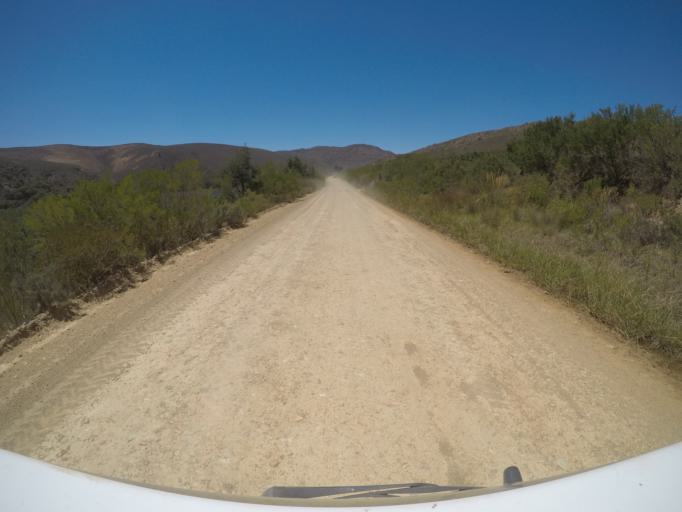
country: ZA
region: Western Cape
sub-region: Overberg District Municipality
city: Grabouw
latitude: -34.1140
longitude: 19.2253
